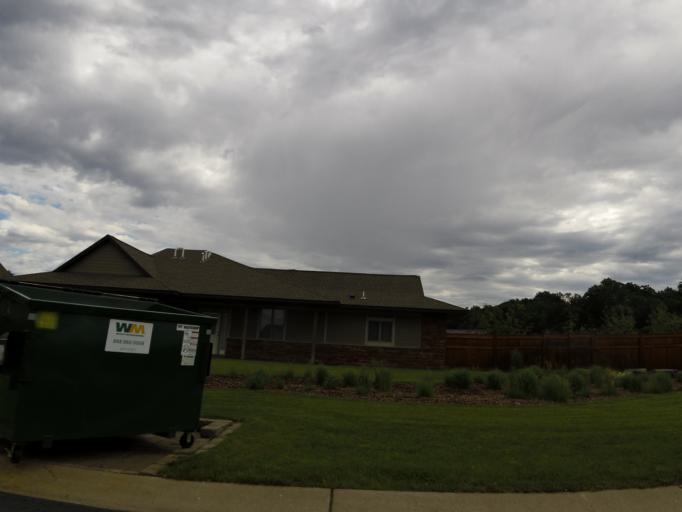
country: US
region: Minnesota
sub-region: Scott County
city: Prior Lake
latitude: 44.7578
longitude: -93.4461
